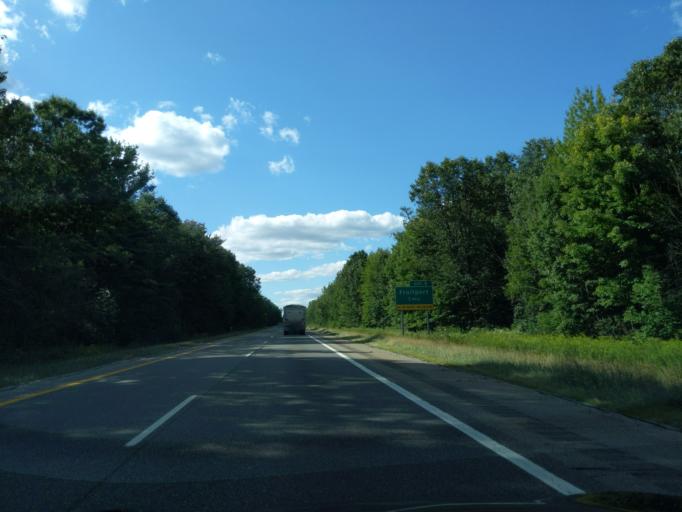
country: US
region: Michigan
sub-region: Muskegon County
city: Fruitport
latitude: 43.1067
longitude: -86.1164
